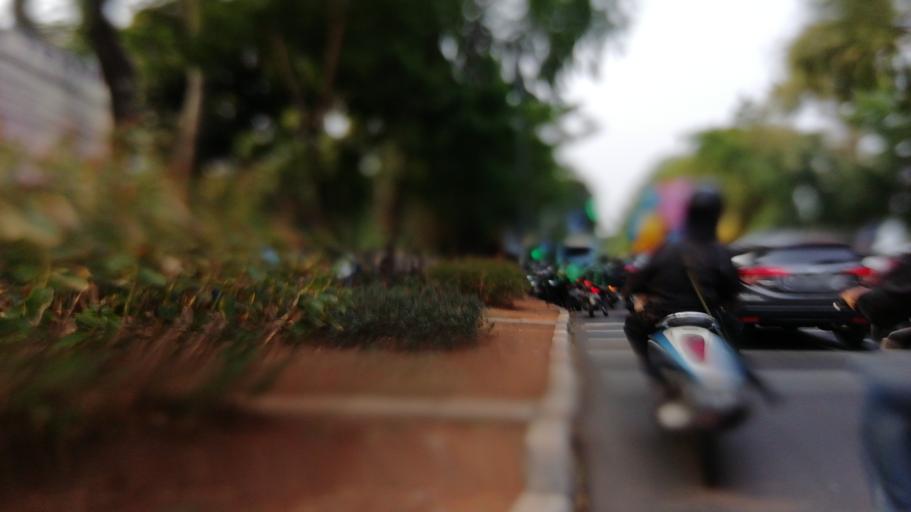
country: ID
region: West Java
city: Depok
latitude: -6.3397
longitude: 106.8339
